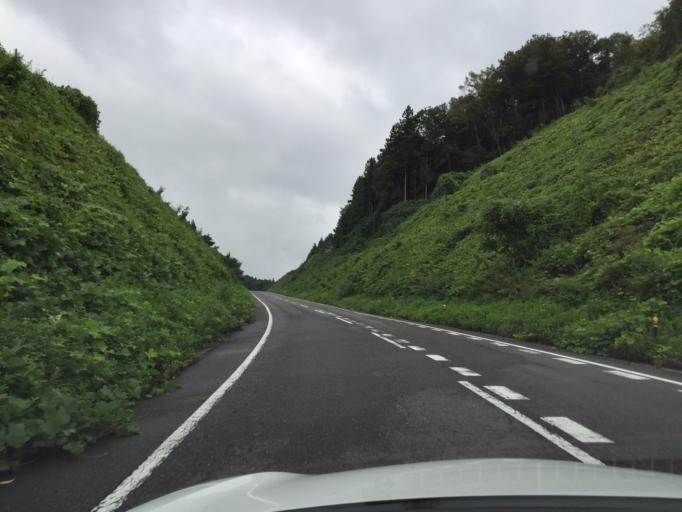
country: JP
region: Fukushima
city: Miharu
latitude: 37.4526
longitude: 140.5251
